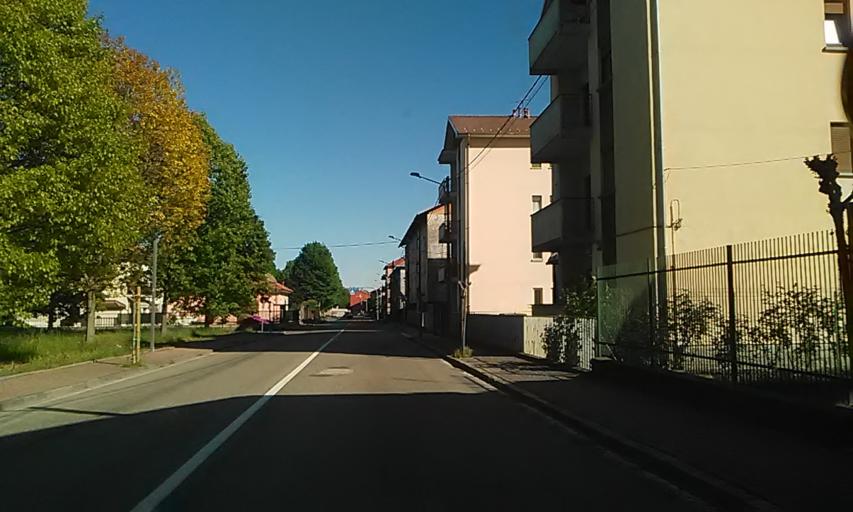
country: IT
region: Piedmont
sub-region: Provincia di Novara
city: Romagnano Sesia
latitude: 45.6300
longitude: 8.3887
